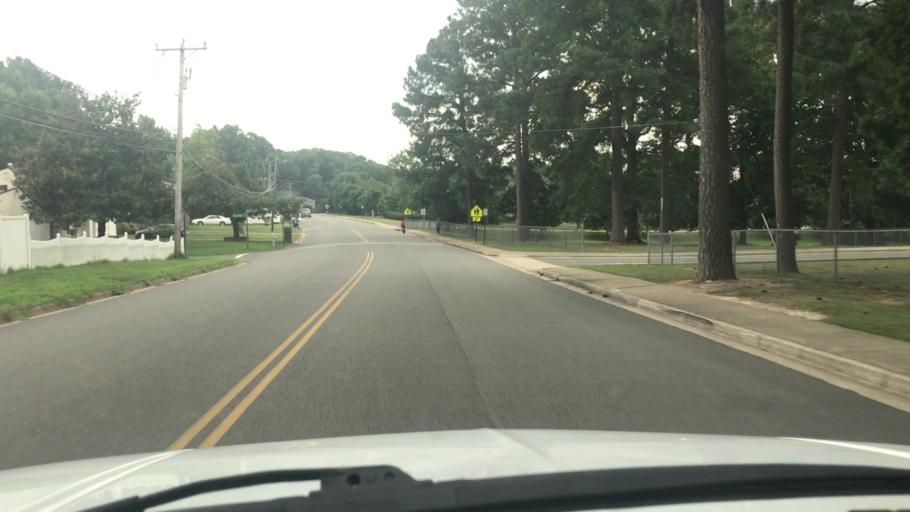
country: US
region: Virginia
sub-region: Henrico County
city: Tuckahoe
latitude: 37.6030
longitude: -77.5893
